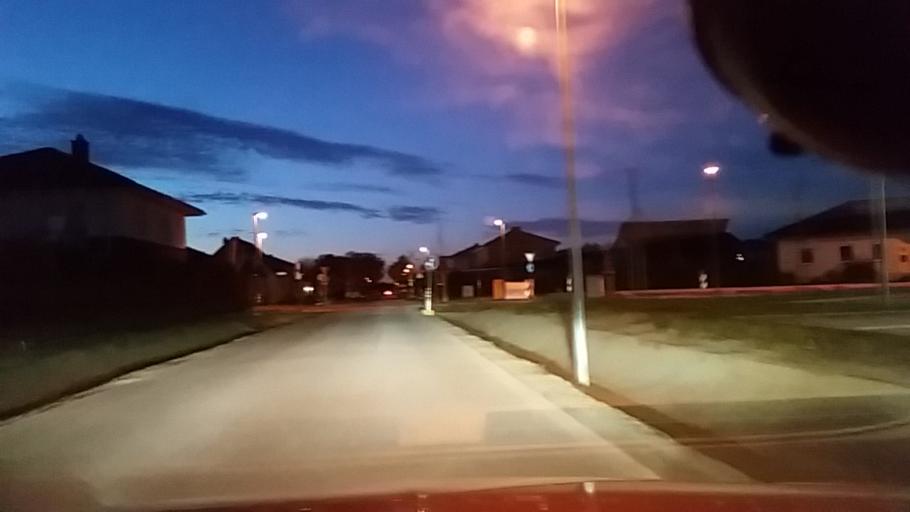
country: DE
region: Lower Saxony
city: Jembke
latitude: 52.4717
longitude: 10.7717
